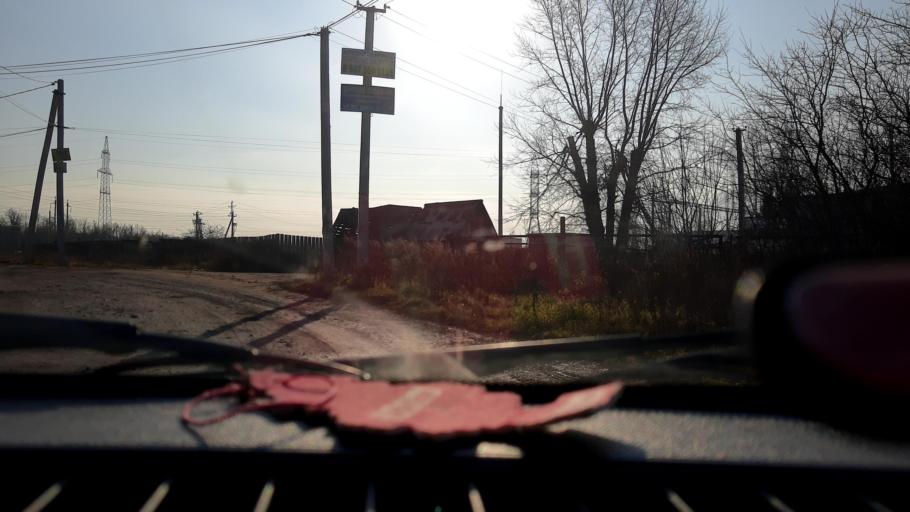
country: RU
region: Bashkortostan
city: Ufa
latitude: 54.6742
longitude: 56.0854
